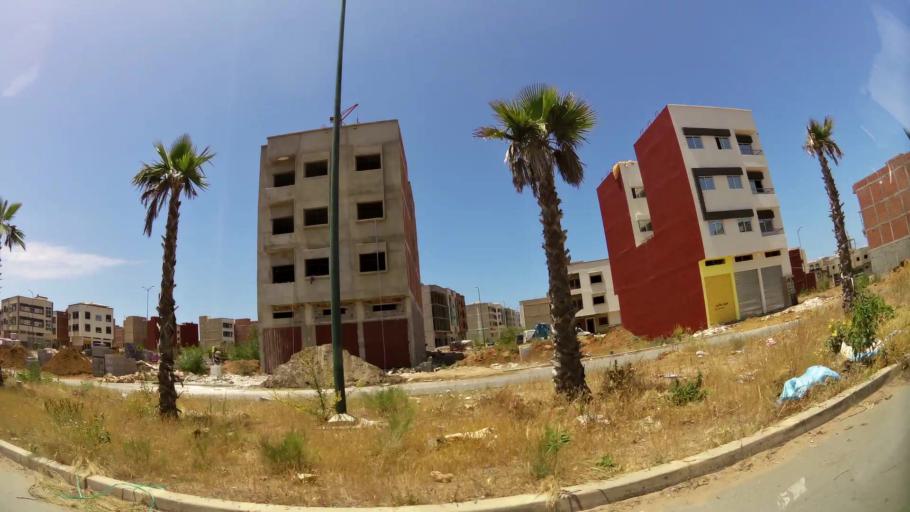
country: MA
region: Gharb-Chrarda-Beni Hssen
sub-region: Kenitra Province
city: Kenitra
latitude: 34.2451
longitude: -6.6516
